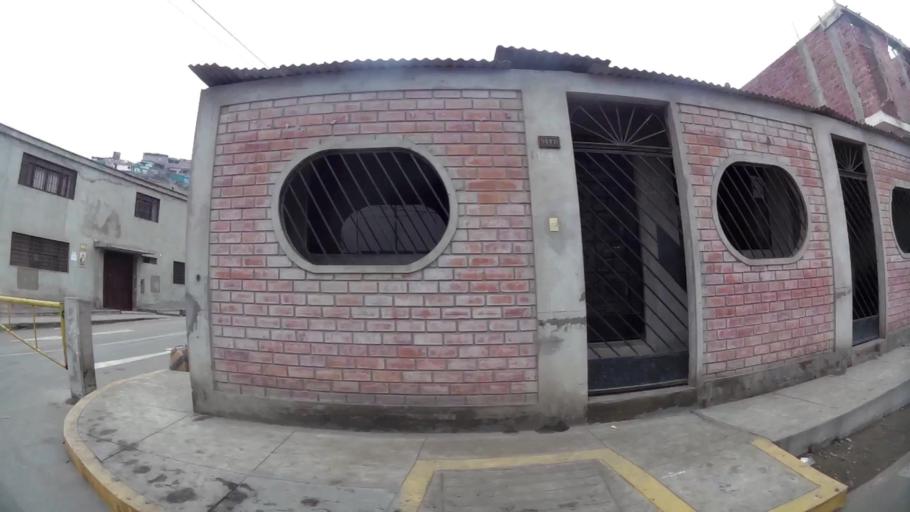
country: PE
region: Lima
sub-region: Lima
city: Surco
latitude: -12.2202
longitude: -76.9101
